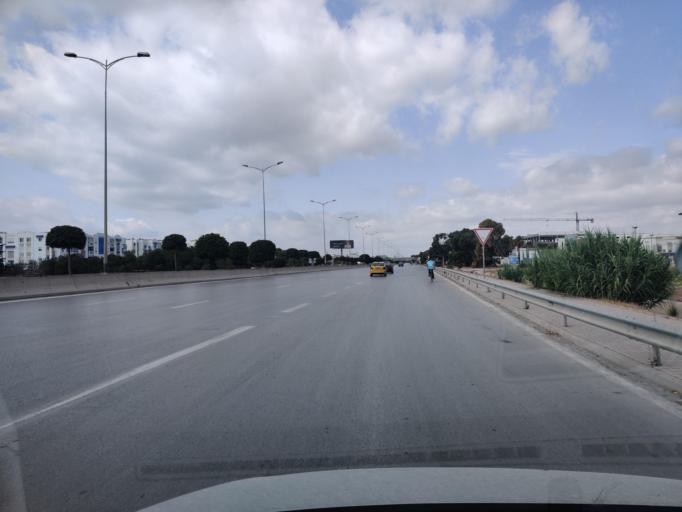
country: TN
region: Tunis
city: Al Marsa
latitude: 36.8698
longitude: 10.3111
